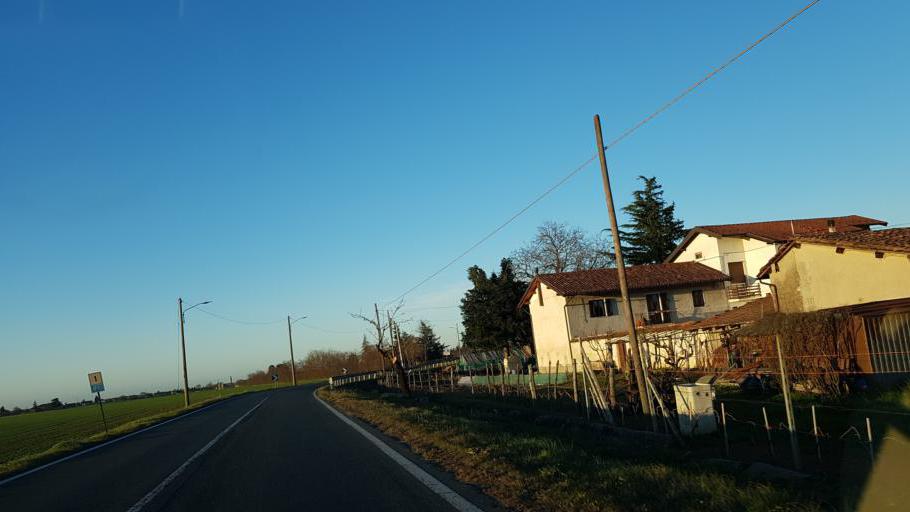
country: IT
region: Piedmont
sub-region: Provincia di Alessandria
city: Villalvernia
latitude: 44.7933
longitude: 8.8284
